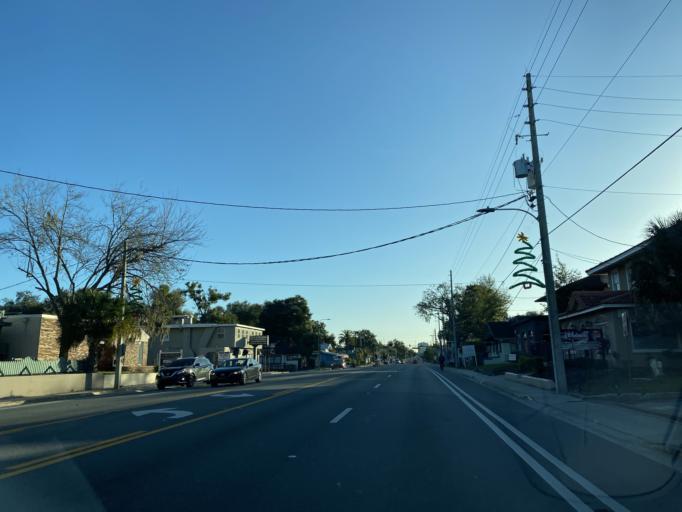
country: US
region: Florida
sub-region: Orange County
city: Orlando
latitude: 28.5530
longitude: -81.3908
